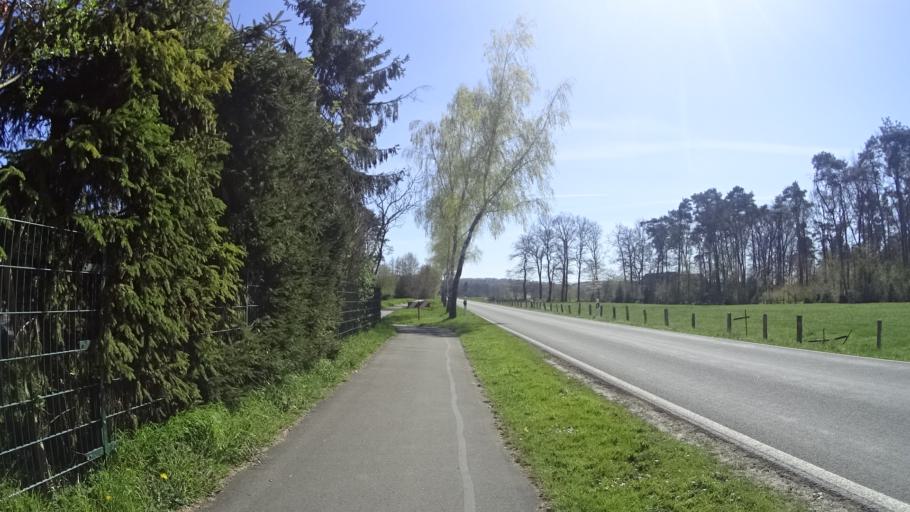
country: DE
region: North Rhine-Westphalia
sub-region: Regierungsbezirk Munster
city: Dulmen
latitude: 51.7872
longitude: 7.2717
